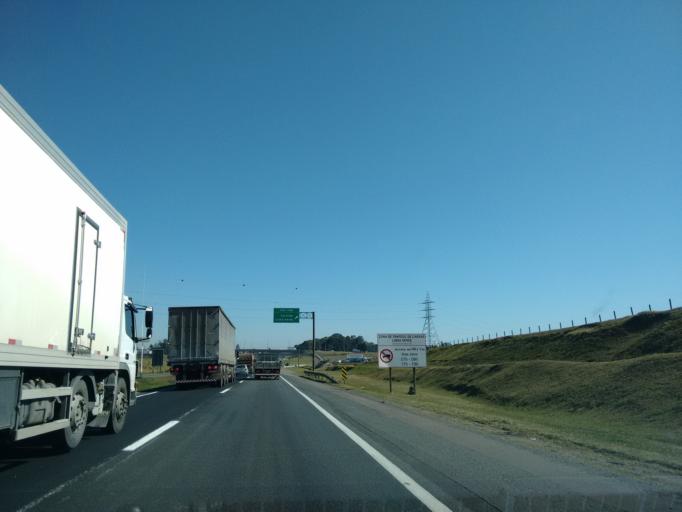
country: BR
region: Parana
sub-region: Sao Jose Dos Pinhais
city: Sao Jose dos Pinhais
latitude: -25.5456
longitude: -49.2964
